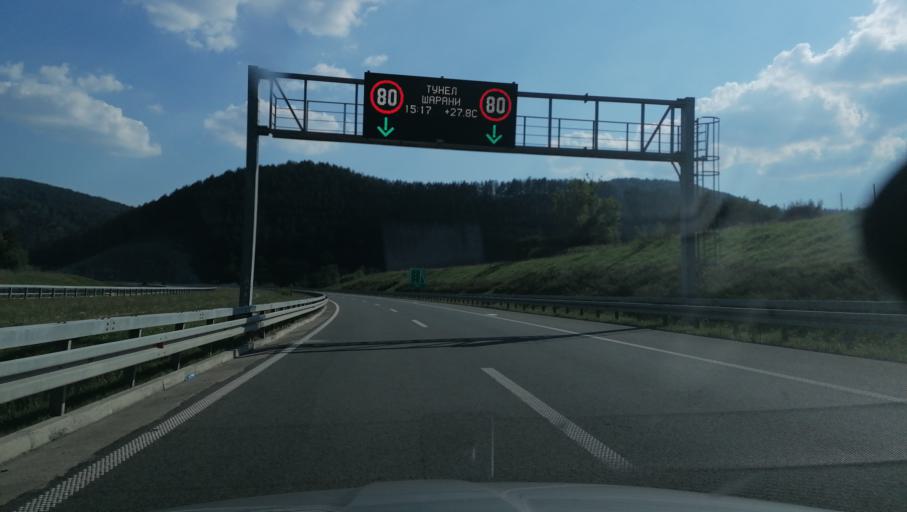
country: RS
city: Prislonica
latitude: 44.0190
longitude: 20.3589
